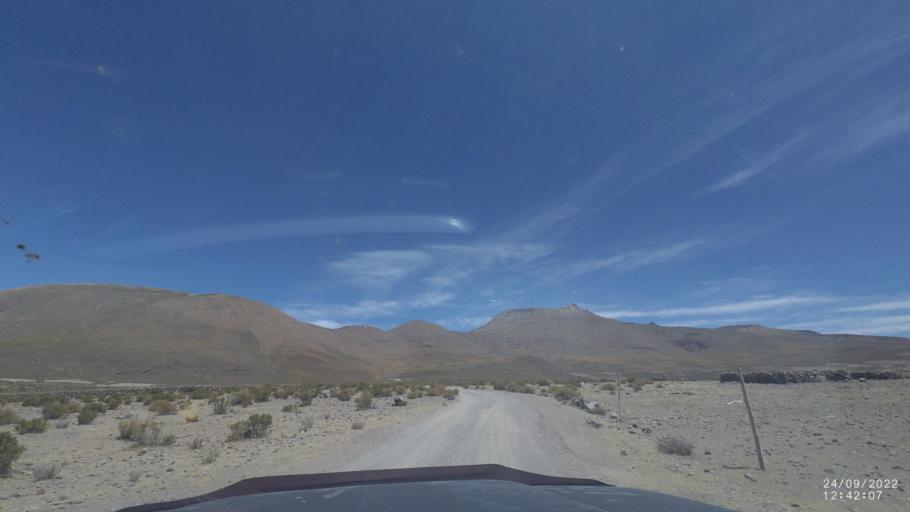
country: BO
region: Potosi
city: Colchani
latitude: -19.7952
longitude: -67.5774
